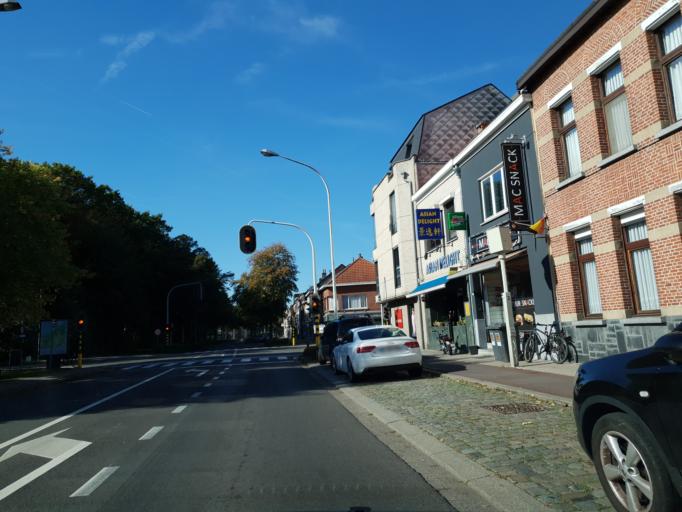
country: BE
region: Flanders
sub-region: Provincie Antwerpen
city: Schoten
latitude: 51.2499
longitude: 4.4864
